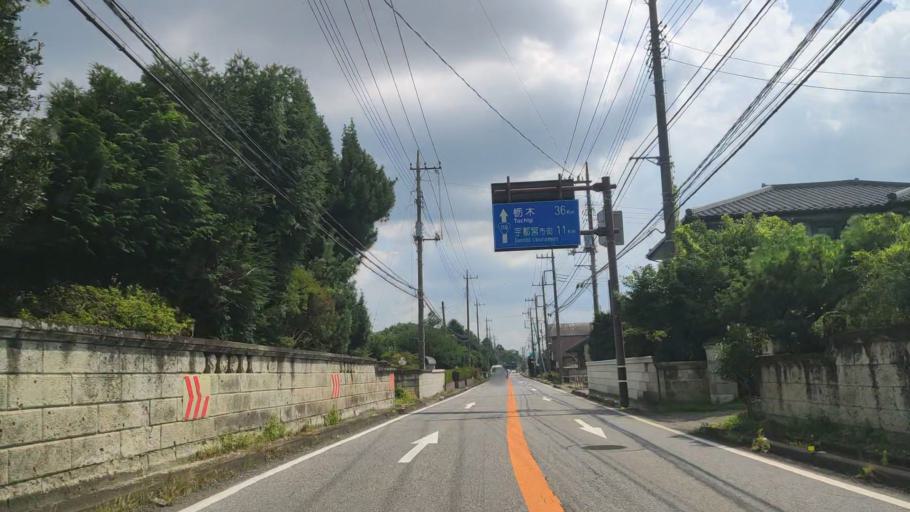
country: JP
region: Tochigi
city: Utsunomiya-shi
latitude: 36.6479
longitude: 139.8461
